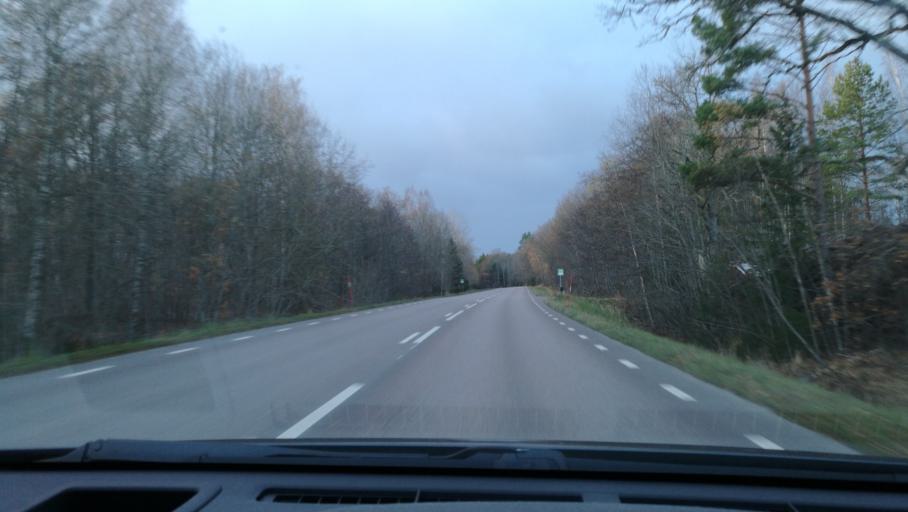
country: SE
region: Soedermanland
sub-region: Vingakers Kommun
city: Vingaker
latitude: 59.1651
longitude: 15.9880
